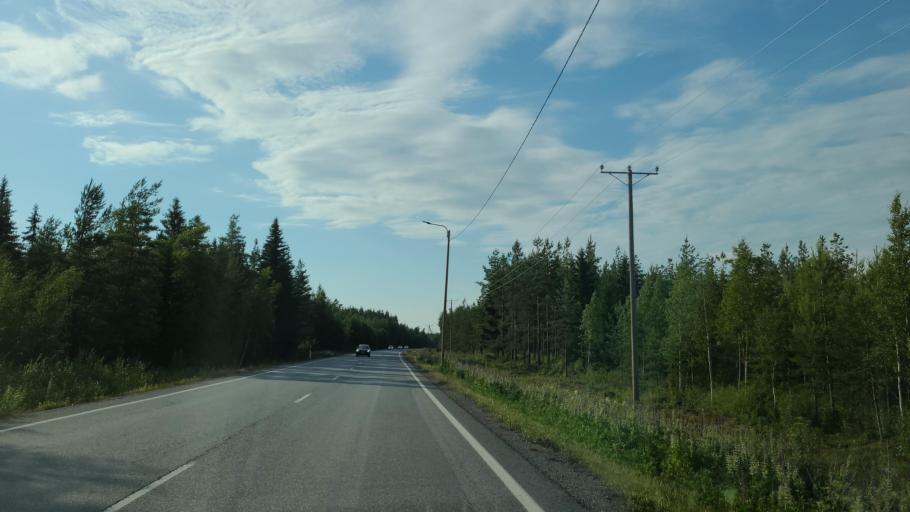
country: FI
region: Ostrobothnia
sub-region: Vaasa
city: Vaasa
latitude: 63.1517
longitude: 21.6007
